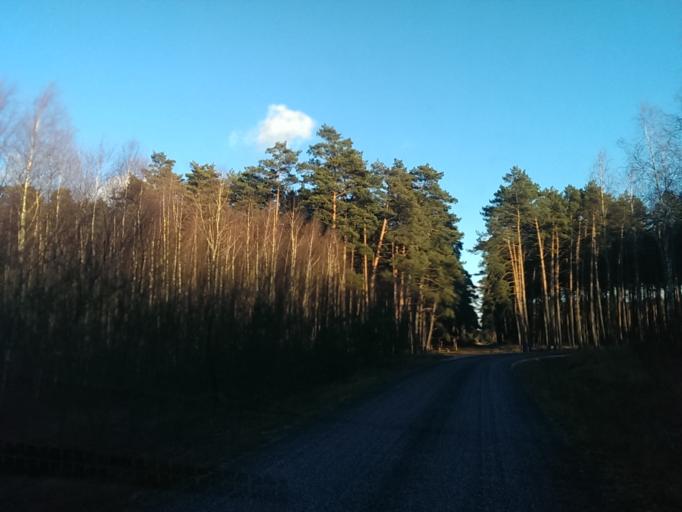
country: PL
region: Kujawsko-Pomorskie
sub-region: Powiat nakielski
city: Naklo nad Notecia
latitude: 53.0583
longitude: 17.5786
